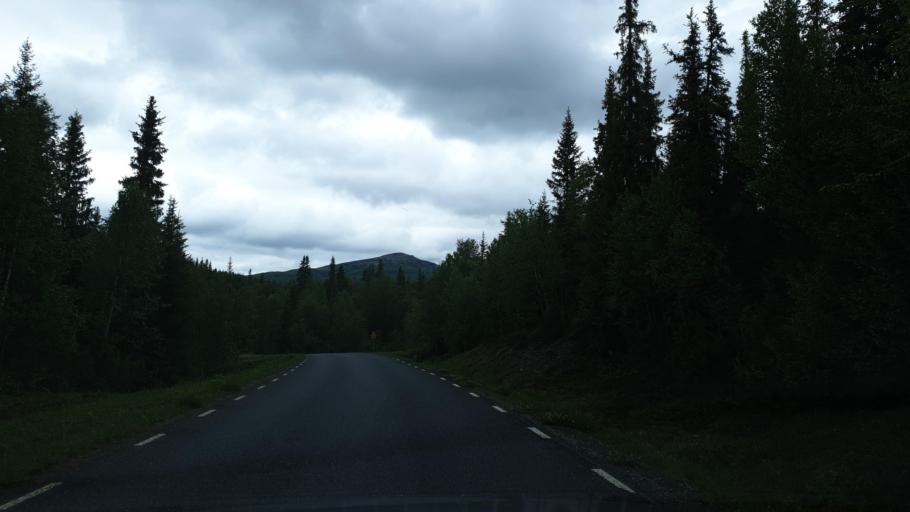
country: SE
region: Vaesterbotten
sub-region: Vilhelmina Kommun
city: Sjoberg
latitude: 65.2741
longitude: 15.3689
